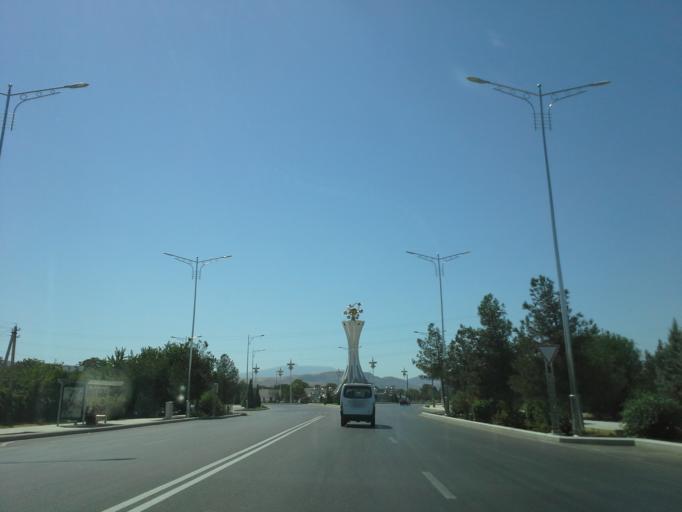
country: TM
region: Ahal
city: Ashgabat
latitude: 37.9307
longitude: 58.2960
